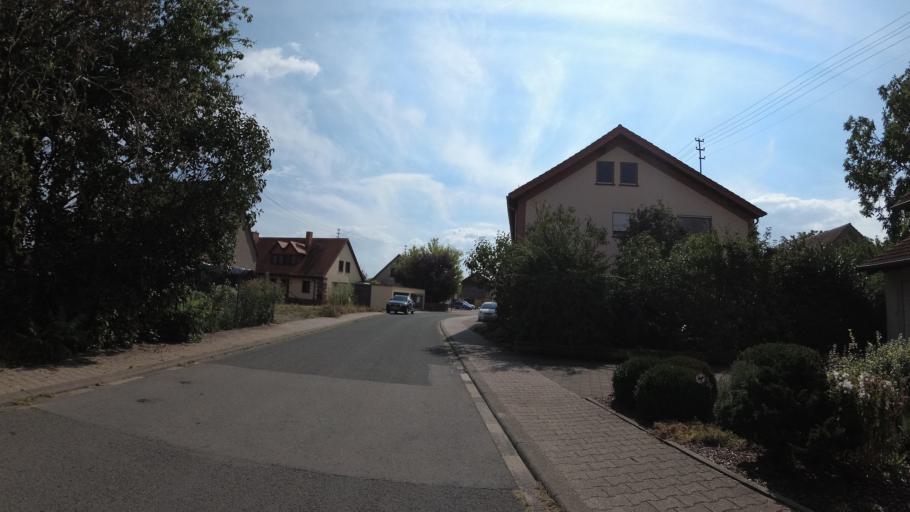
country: DE
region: Rheinland-Pfalz
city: Rosenkopf
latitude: 49.3453
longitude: 7.4353
